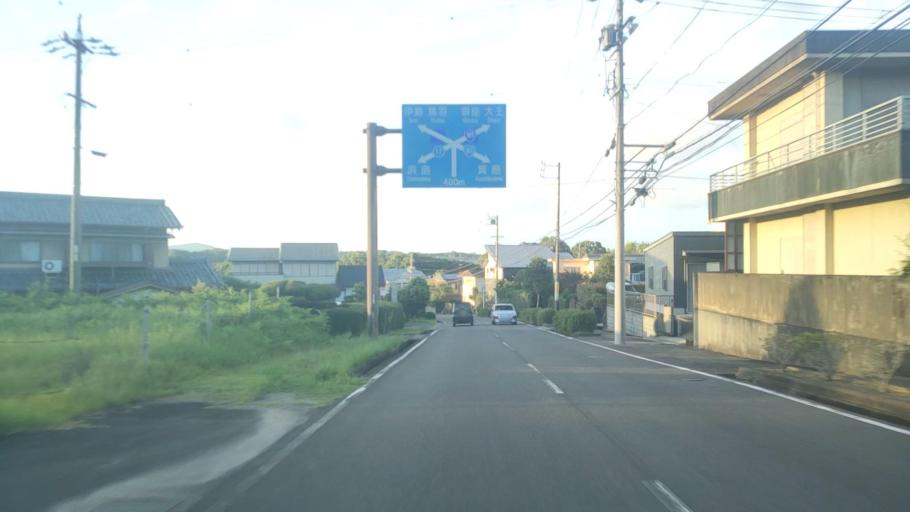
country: JP
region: Mie
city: Toba
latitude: 34.3250
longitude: 136.8222
